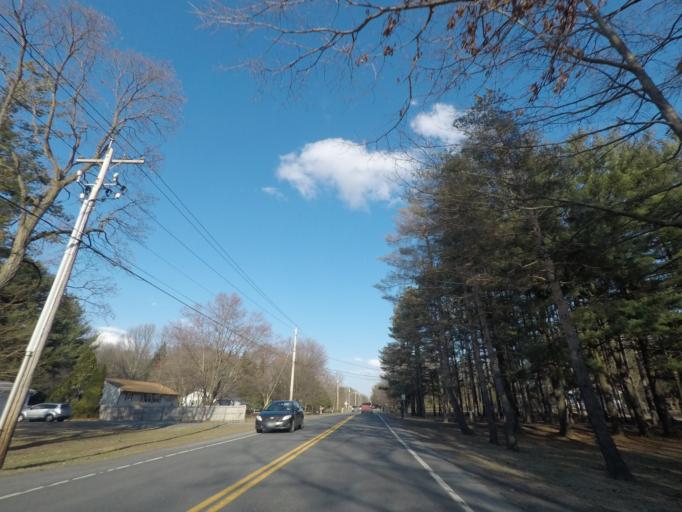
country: US
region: New York
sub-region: Saratoga County
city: Country Knolls
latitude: 42.8551
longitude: -73.7903
